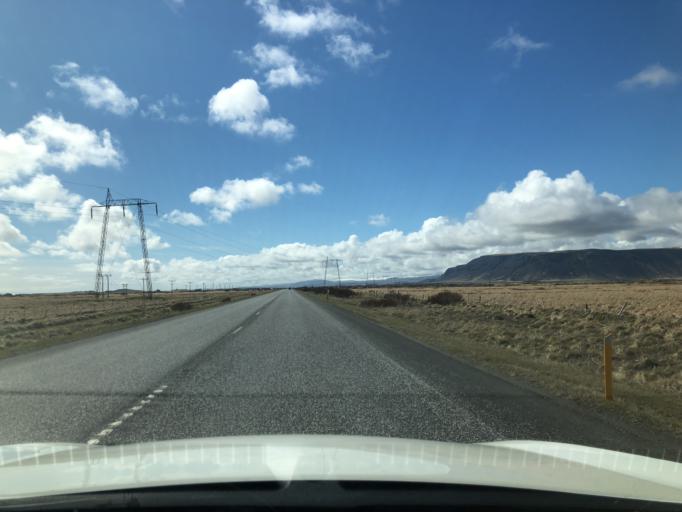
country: IS
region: South
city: Selfoss
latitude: 63.9431
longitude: -20.8710
